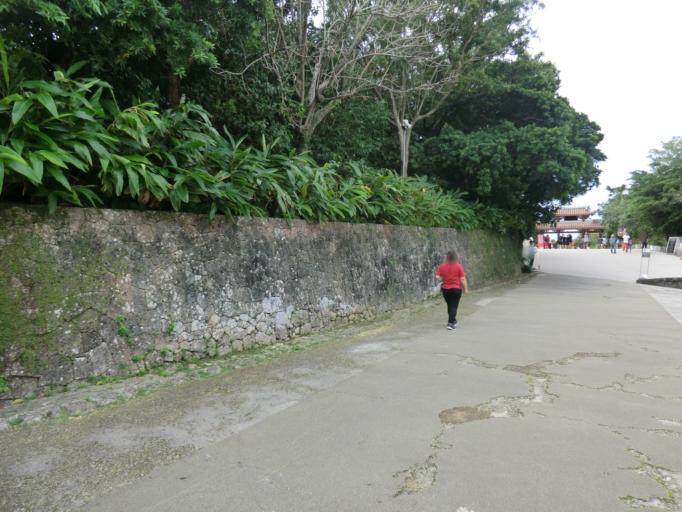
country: JP
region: Okinawa
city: Naha-shi
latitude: 26.2180
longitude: 127.7176
